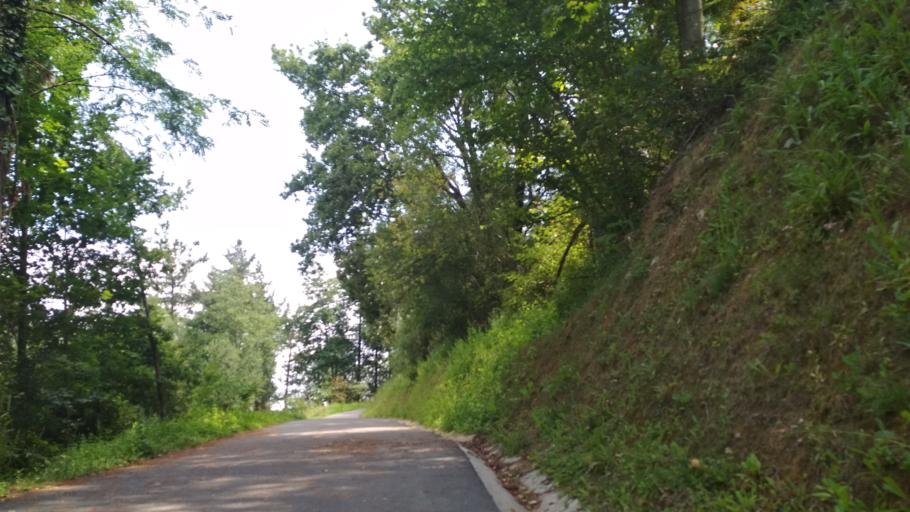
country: ES
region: Basque Country
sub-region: Provincia de Guipuzcoa
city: San Sebastian
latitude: 43.2968
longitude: -1.9810
